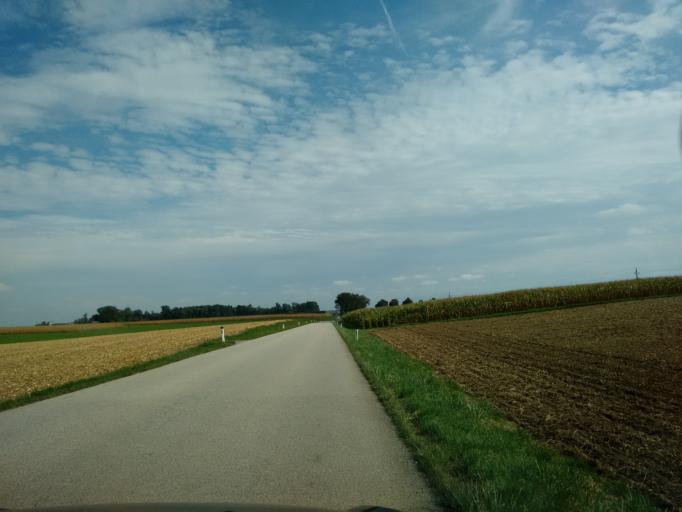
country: AT
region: Upper Austria
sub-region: Wels-Land
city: Marchtrenk
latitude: 48.1263
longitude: 14.1095
